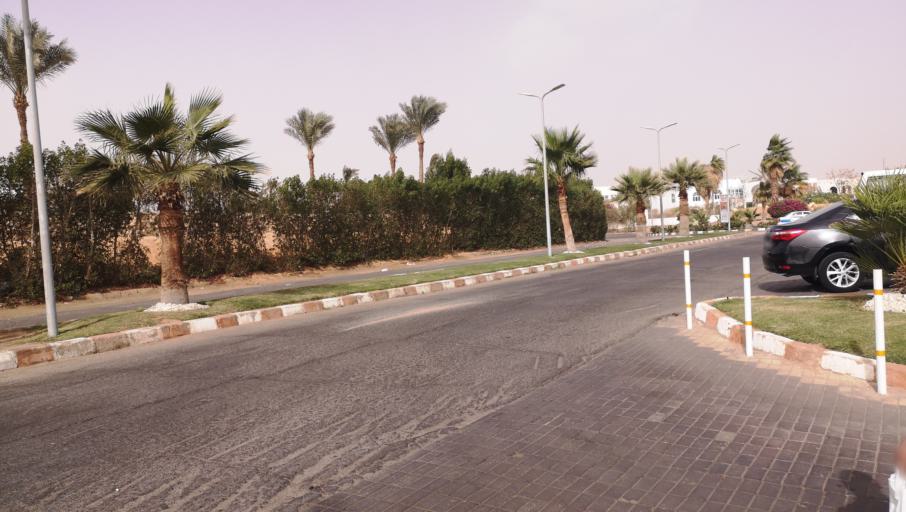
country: EG
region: South Sinai
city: Sharm el-Sheikh
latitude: 27.8646
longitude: 34.3162
